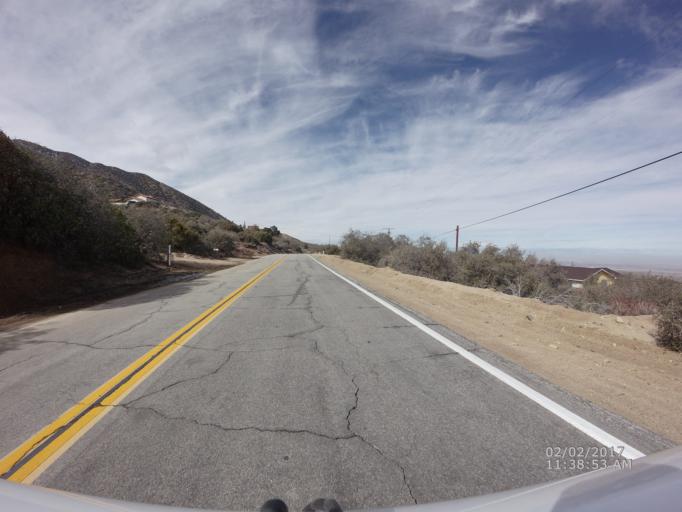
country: US
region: California
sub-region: Los Angeles County
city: Littlerock
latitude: 34.4324
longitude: -117.9244
